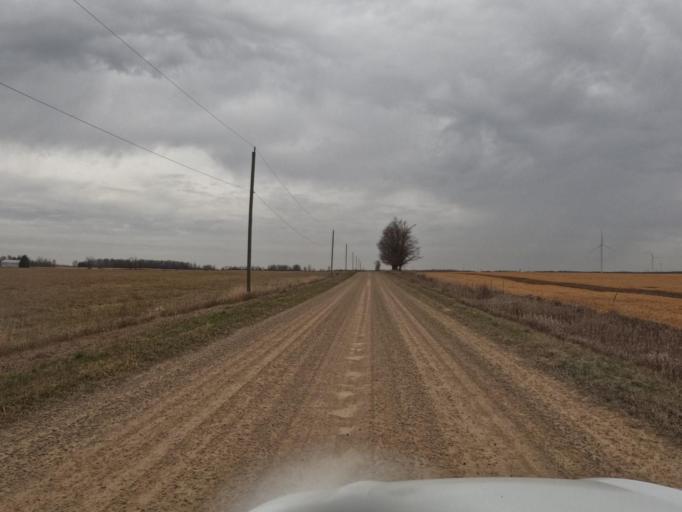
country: CA
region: Ontario
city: Shelburne
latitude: 43.8810
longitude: -80.3810
